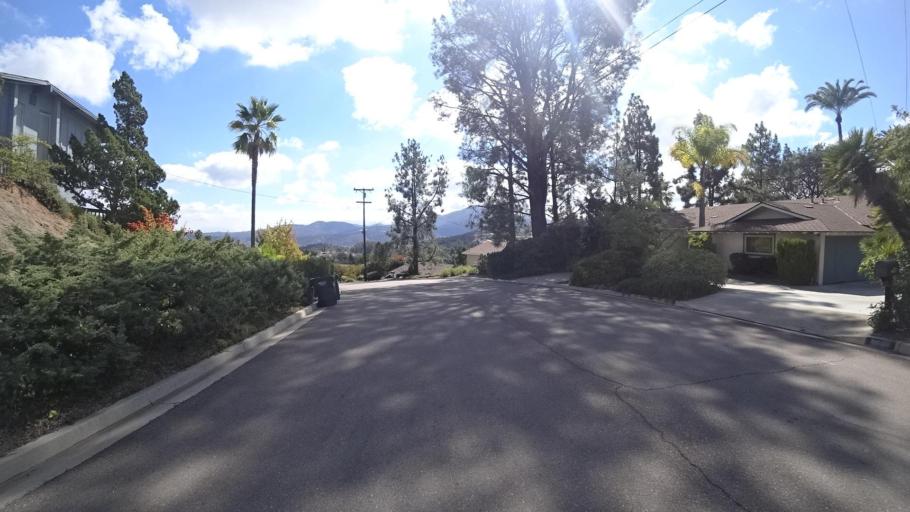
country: US
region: California
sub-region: San Diego County
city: Rancho San Diego
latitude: 32.7637
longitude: -116.9466
